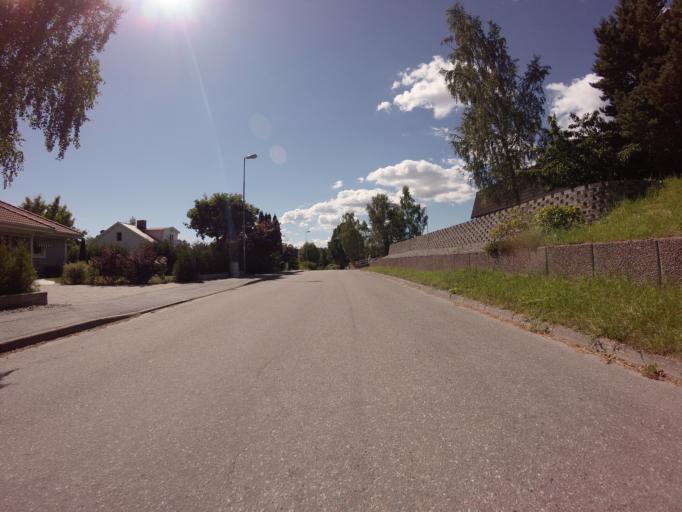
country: SE
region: Stockholm
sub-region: Sollentuna Kommun
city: Sollentuna
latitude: 59.4525
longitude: 17.8954
